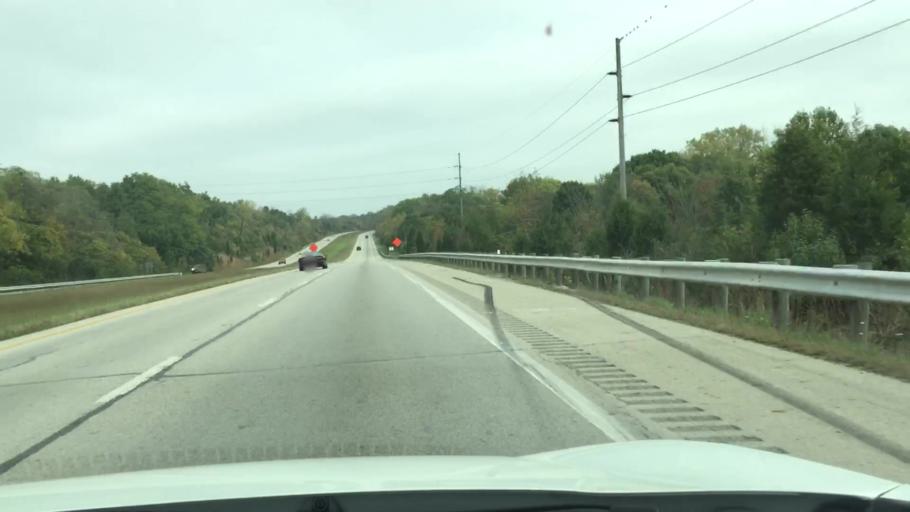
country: US
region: Ohio
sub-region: Greene County
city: Wright-Patterson AFB
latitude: 39.8061
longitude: -84.0936
